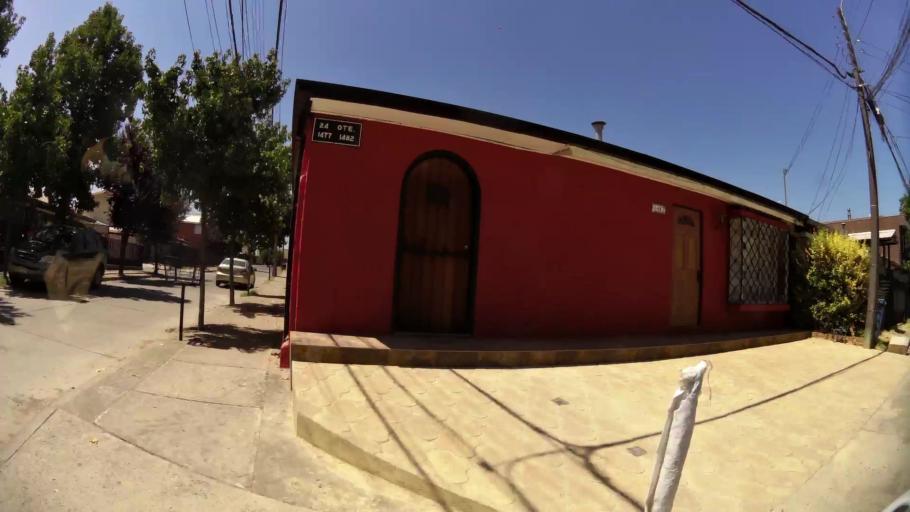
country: CL
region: Maule
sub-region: Provincia de Talca
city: Talca
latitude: -35.4278
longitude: -71.6306
